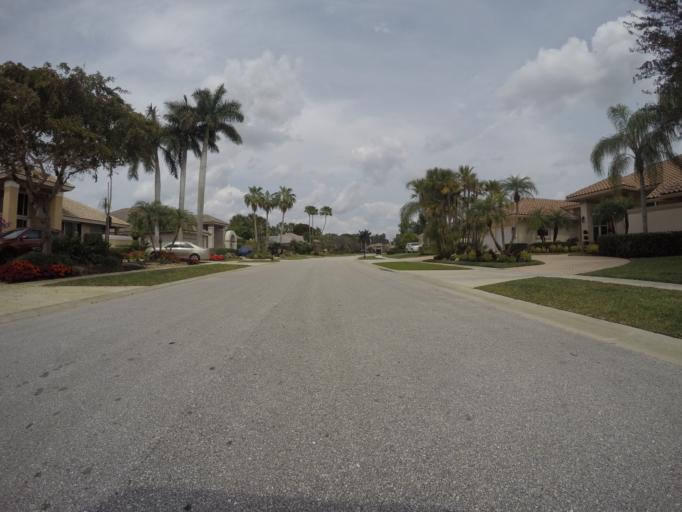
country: US
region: Florida
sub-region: Palm Beach County
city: Villages of Oriole
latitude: 26.4141
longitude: -80.2215
